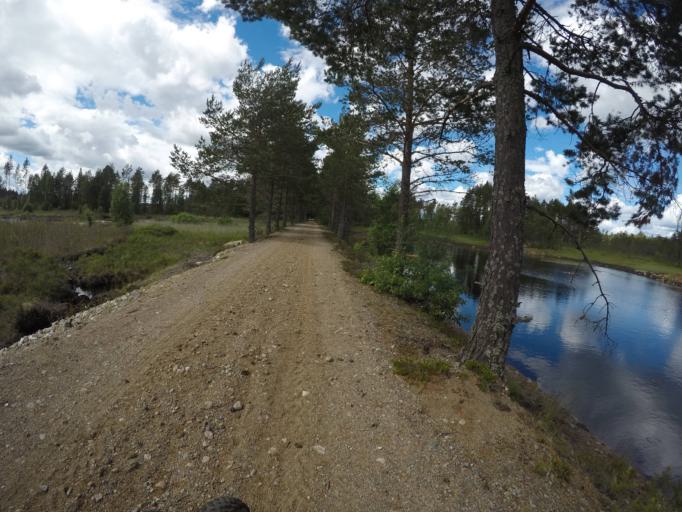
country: SE
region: Vaermland
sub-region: Filipstads Kommun
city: Lesjofors
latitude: 60.1389
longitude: 14.2650
